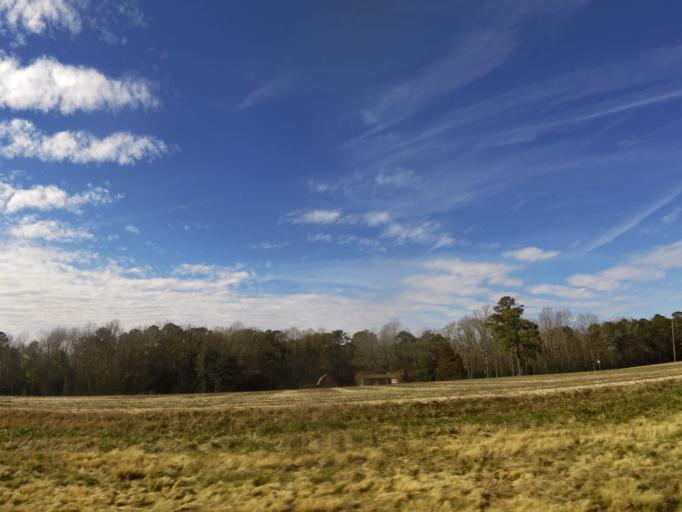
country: US
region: Virginia
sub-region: City of Franklin
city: Franklin
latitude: 36.7596
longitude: -76.8596
